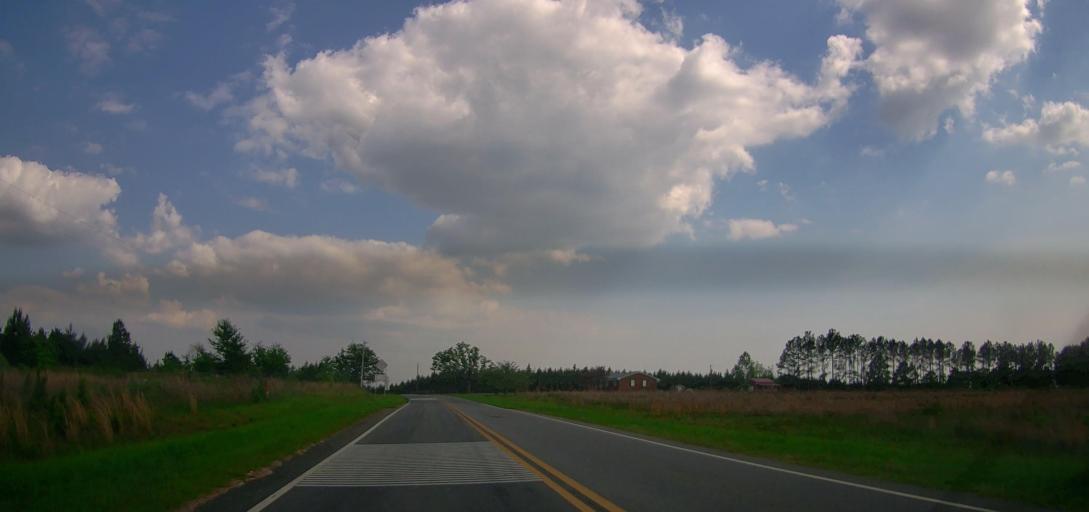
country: US
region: Georgia
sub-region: Laurens County
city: East Dublin
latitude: 32.6218
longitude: -82.8776
